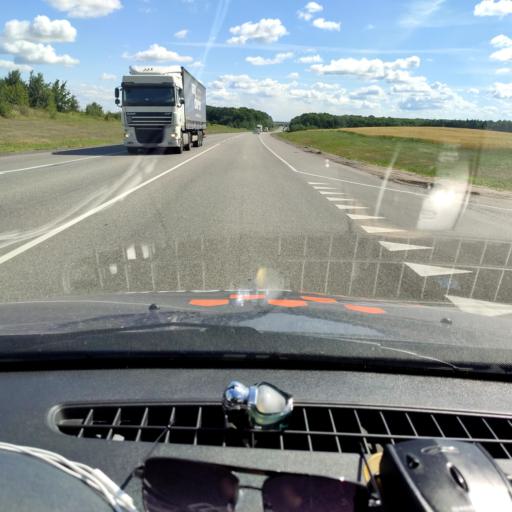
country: RU
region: Lipetsk
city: Borinskoye
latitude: 52.4687
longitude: 39.3465
